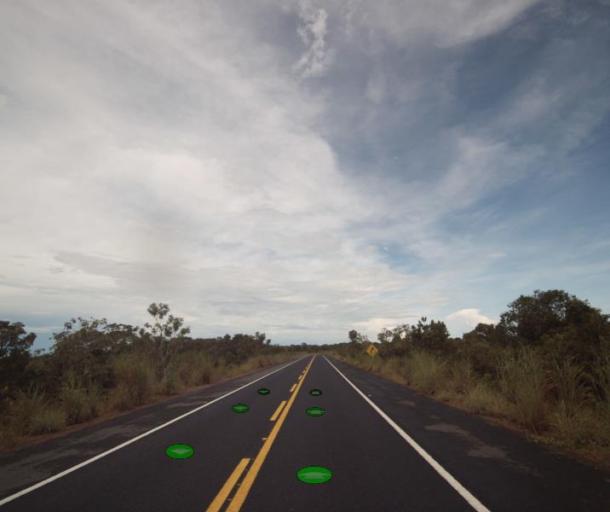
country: BR
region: Goias
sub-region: Sao Miguel Do Araguaia
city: Sao Miguel do Araguaia
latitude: -13.2395
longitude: -50.5441
